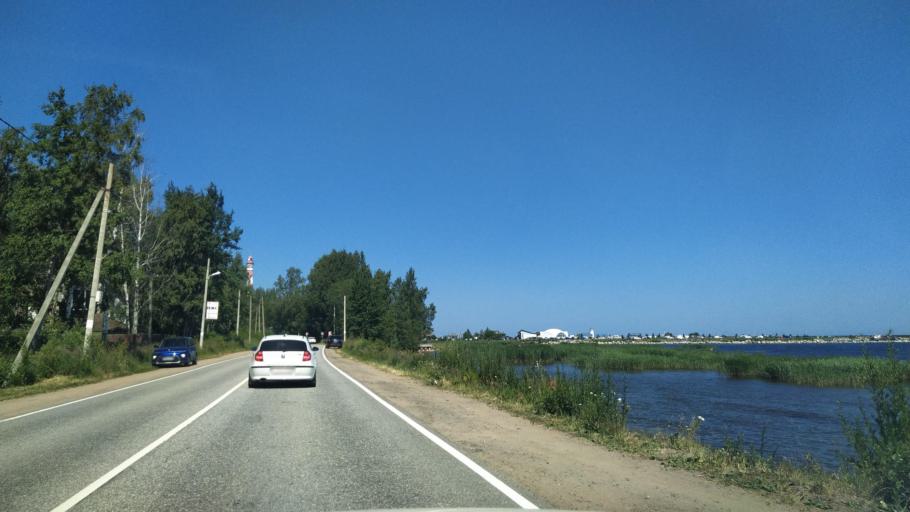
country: RU
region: Leningrad
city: Borisova Griva
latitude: 60.1136
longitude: 31.0839
